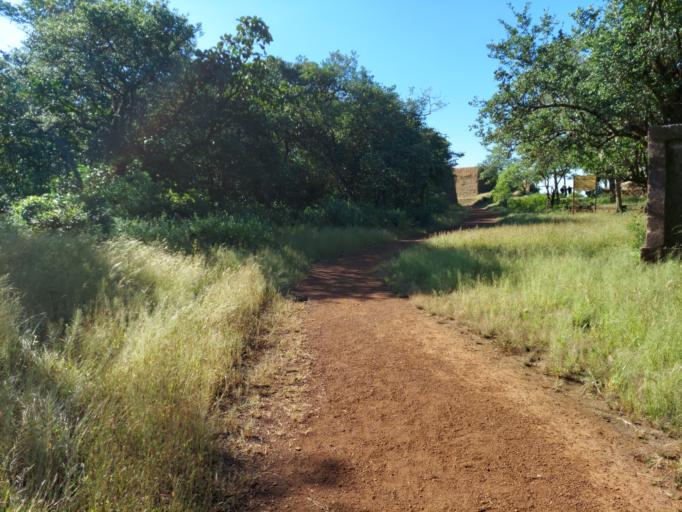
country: IN
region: Maharashtra
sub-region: Sindhudurg
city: Kudal
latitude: 16.0842
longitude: 73.8439
